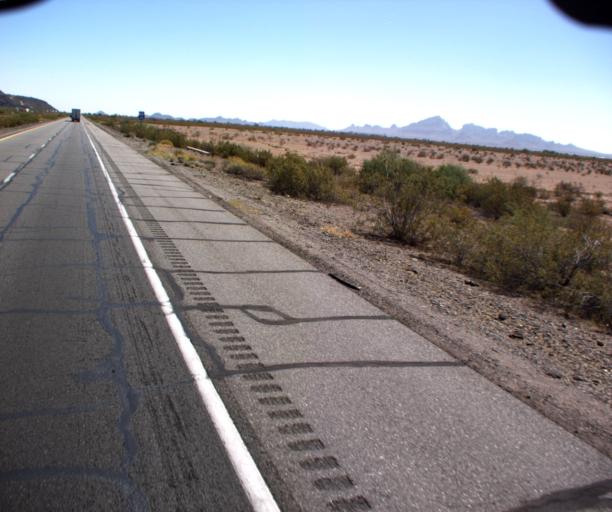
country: US
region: Arizona
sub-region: La Paz County
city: Salome
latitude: 33.5347
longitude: -113.1437
